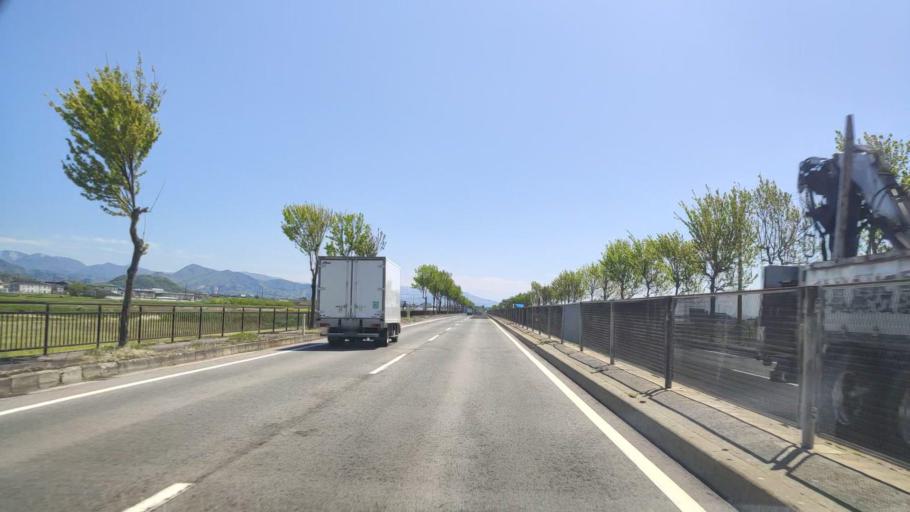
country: JP
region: Yamagata
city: Higashine
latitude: 38.4656
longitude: 140.3826
